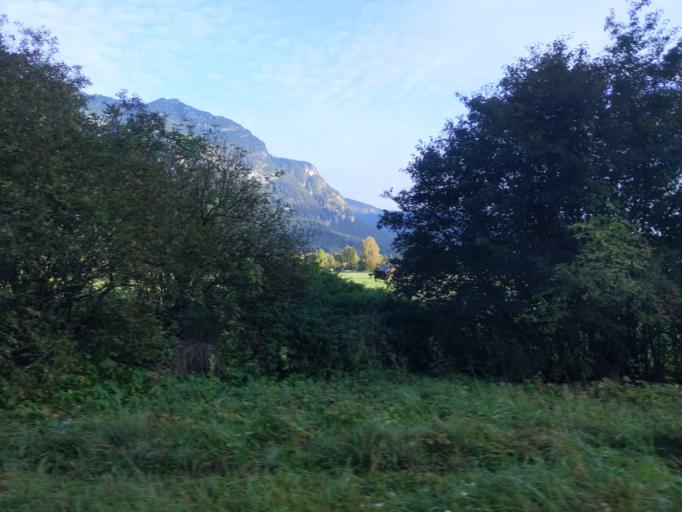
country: DE
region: Bavaria
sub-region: Upper Bavaria
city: Garmisch-Partenkirchen
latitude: 47.4816
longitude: 11.0812
